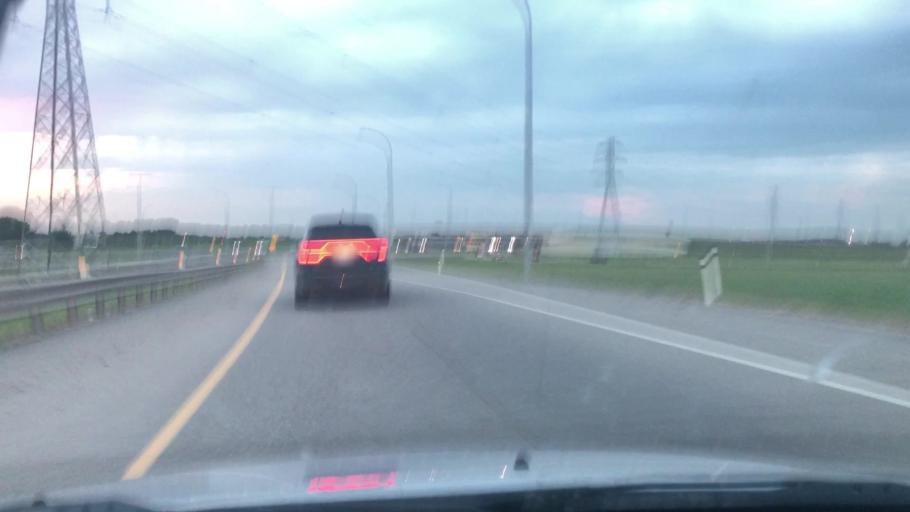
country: CA
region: Alberta
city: St. Albert
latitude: 53.5190
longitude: -113.6573
